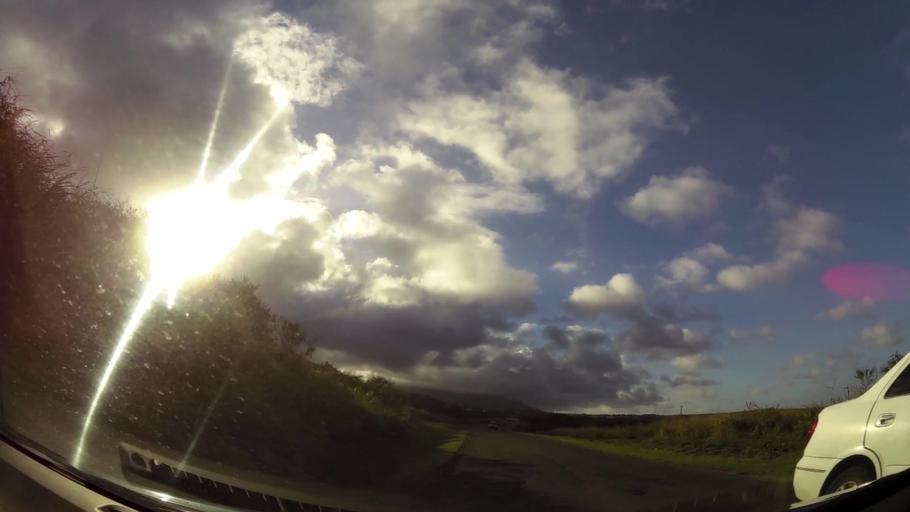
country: KN
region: Saint Mary Cayon
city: Cayon
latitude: 17.3466
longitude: -62.7212
